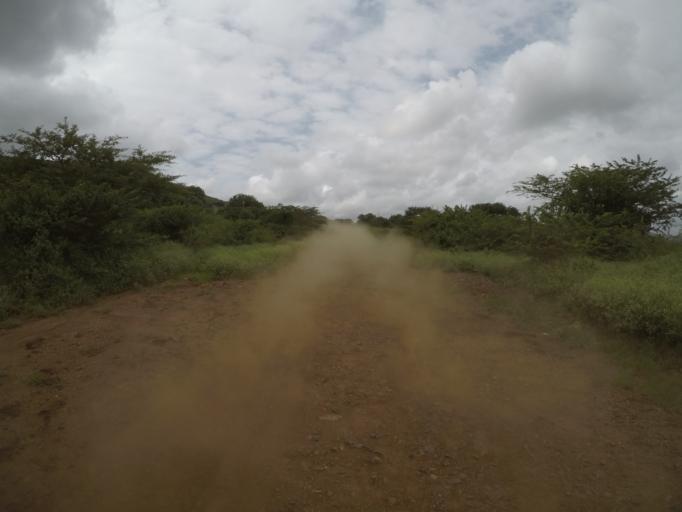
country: ZA
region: KwaZulu-Natal
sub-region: uThungulu District Municipality
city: Empangeni
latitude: -28.6026
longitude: 31.8937
